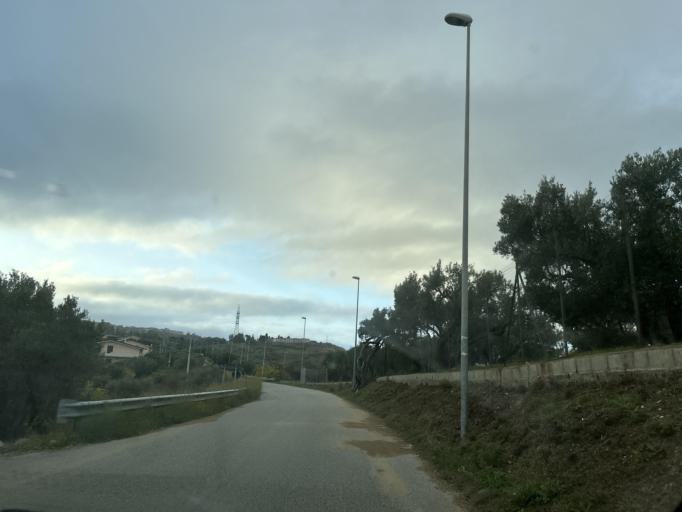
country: IT
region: Calabria
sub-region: Provincia di Catanzaro
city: Staletti
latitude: 38.7638
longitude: 16.5557
